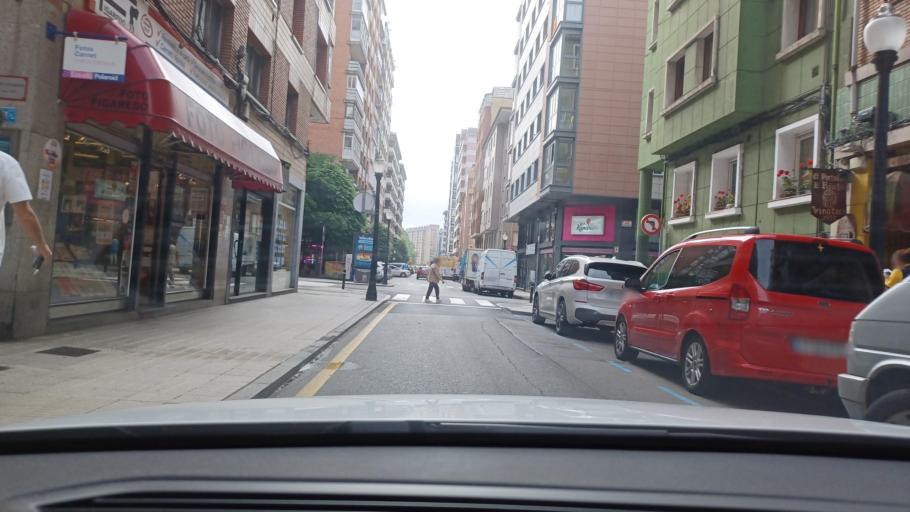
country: ES
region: Asturias
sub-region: Province of Asturias
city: Gijon
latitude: 43.5385
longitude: -5.6486
